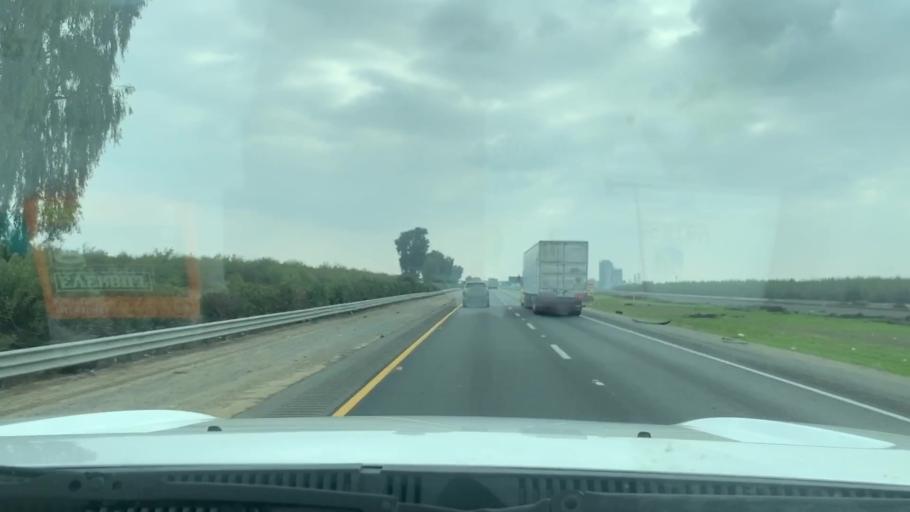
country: US
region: California
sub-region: Tulare County
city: Tipton
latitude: 36.0199
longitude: -119.3053
